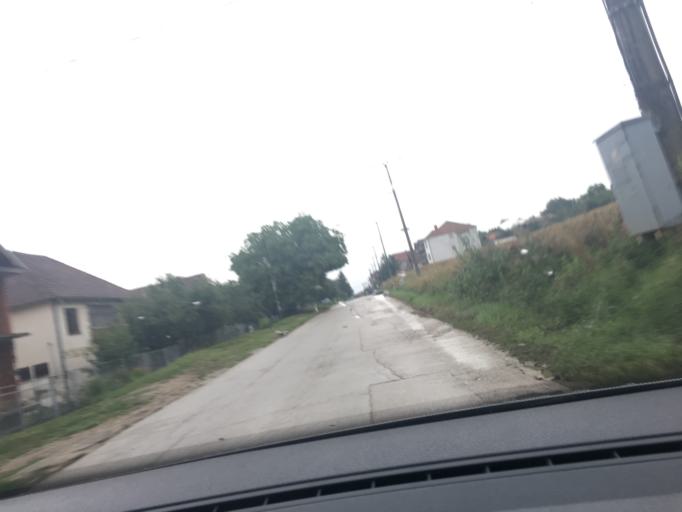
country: RS
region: Central Serbia
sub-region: Nisavski Okrug
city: Aleksinac
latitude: 43.5548
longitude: 21.7051
